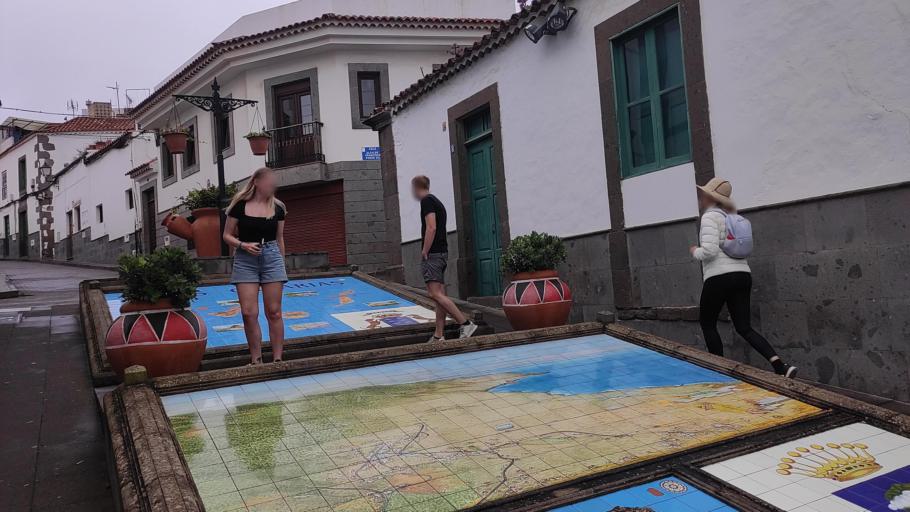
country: ES
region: Canary Islands
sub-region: Provincia de Las Palmas
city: Firgas
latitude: 28.1070
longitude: -15.5633
